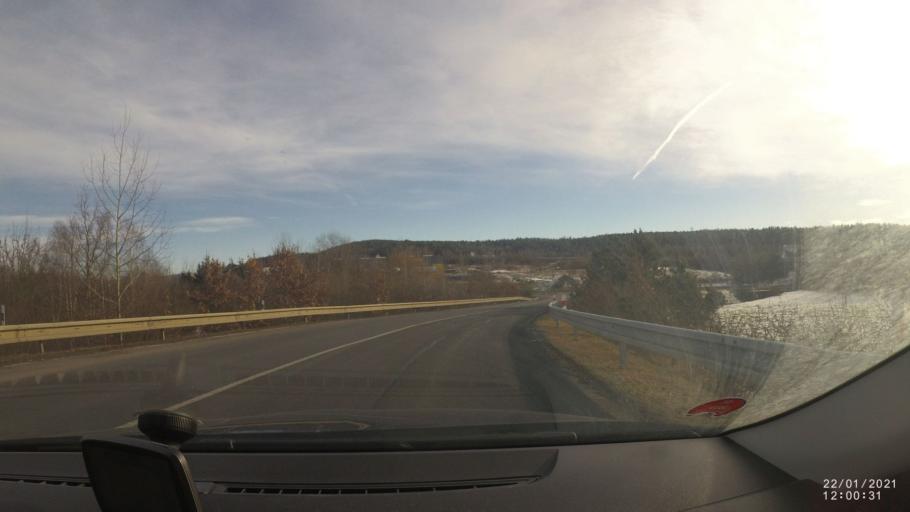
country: CZ
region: Plzensky
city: Dysina
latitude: 49.7395
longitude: 13.5067
